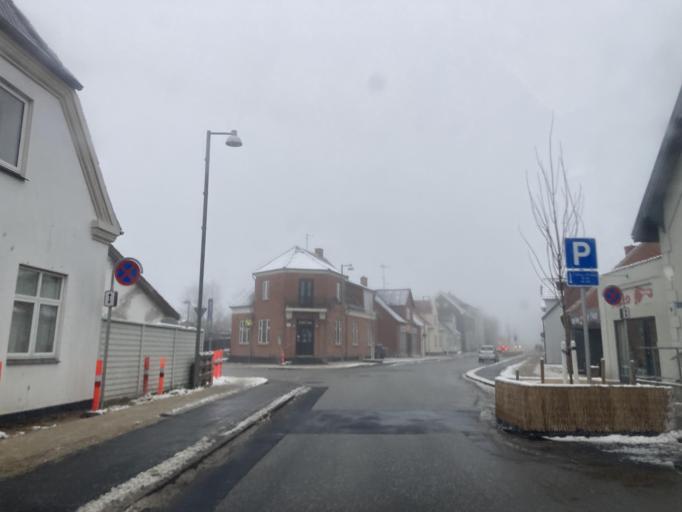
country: DK
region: Zealand
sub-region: Soro Kommune
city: Stenlille
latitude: 55.5401
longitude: 11.5908
